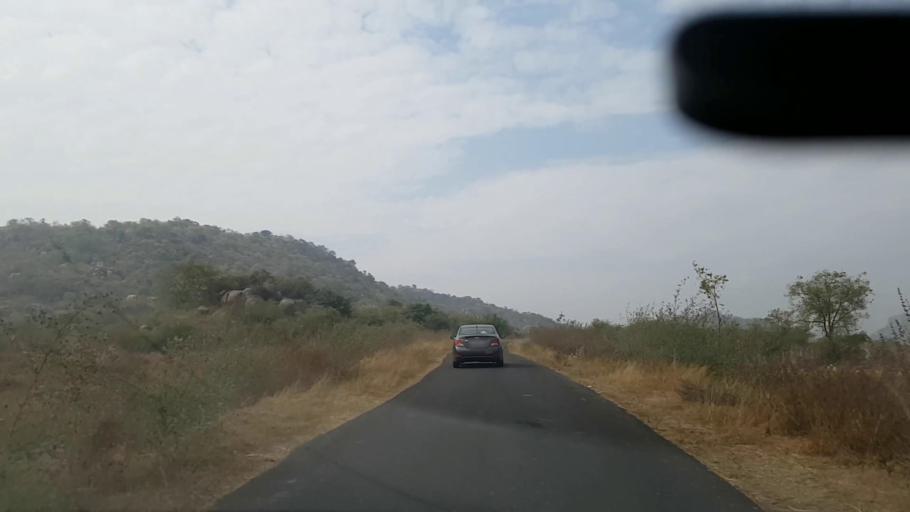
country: IN
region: Telangana
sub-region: Rangareddi
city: Ghatkesar
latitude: 17.1734
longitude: 78.8191
